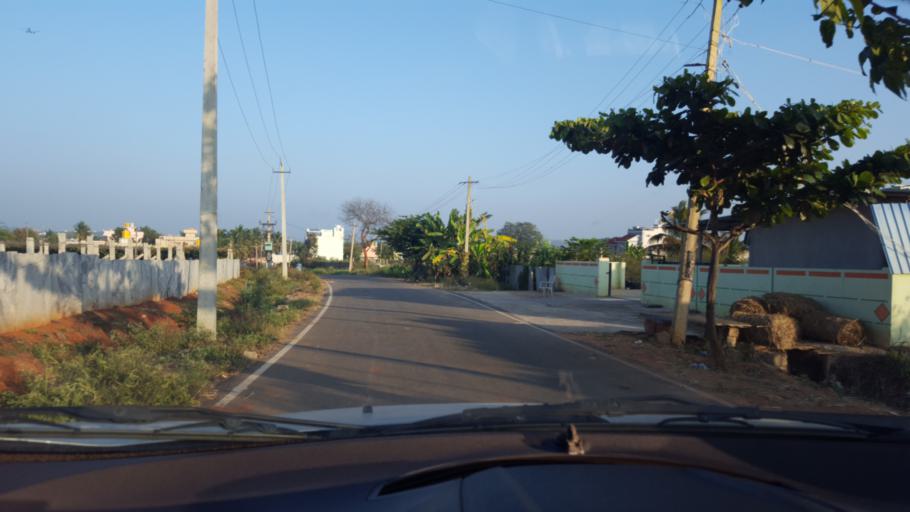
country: IN
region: Karnataka
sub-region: Bangalore Urban
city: Yelahanka
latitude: 13.1879
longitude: 77.6060
